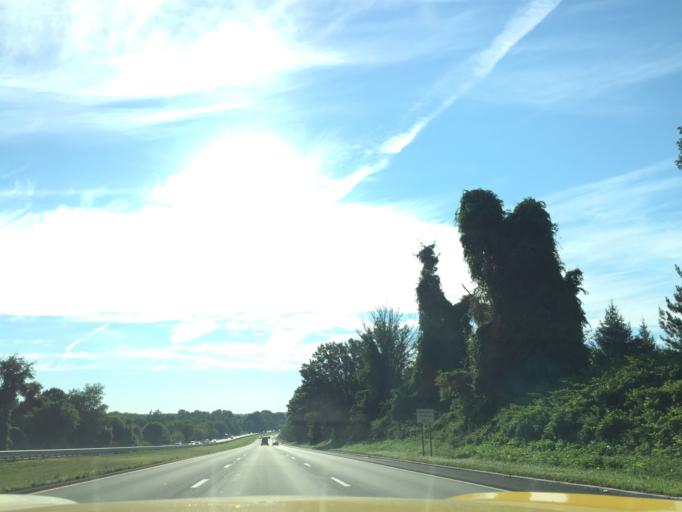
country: US
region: New Jersey
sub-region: Hunterdon County
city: Lebanon
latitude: 40.6466
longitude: -74.8474
